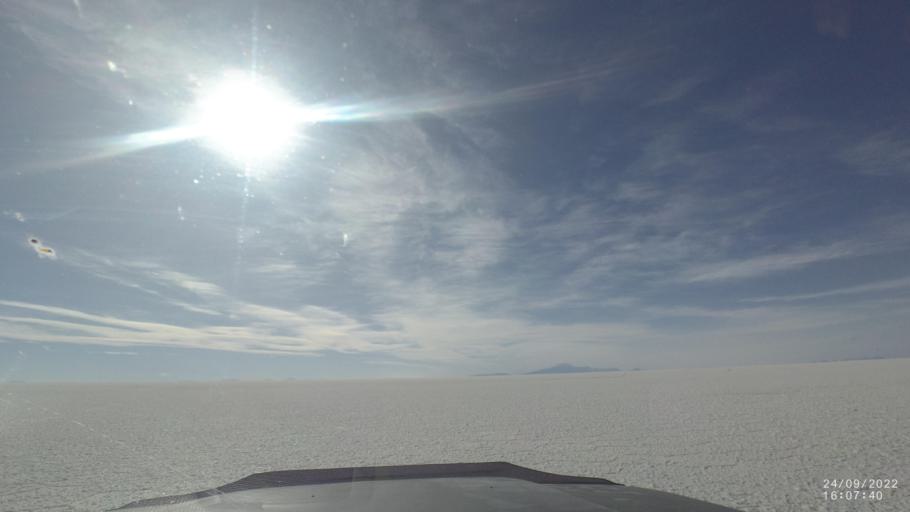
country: BO
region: Potosi
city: Colchani
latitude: -20.2981
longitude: -67.3045
